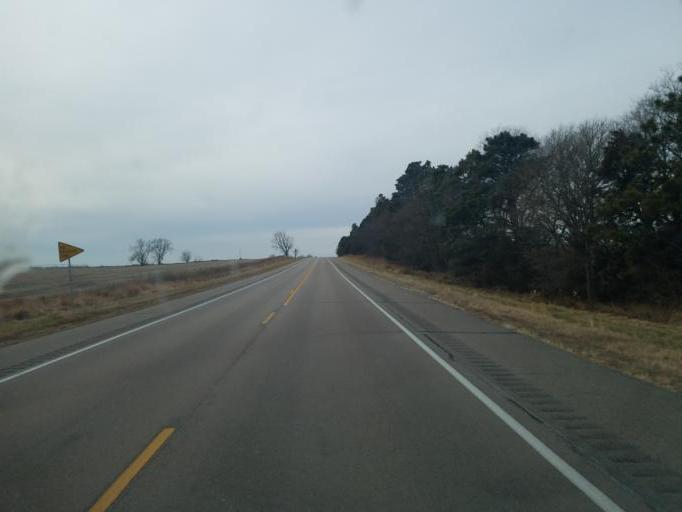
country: US
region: Nebraska
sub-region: Antelope County
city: Neligh
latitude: 42.3351
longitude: -98.1881
